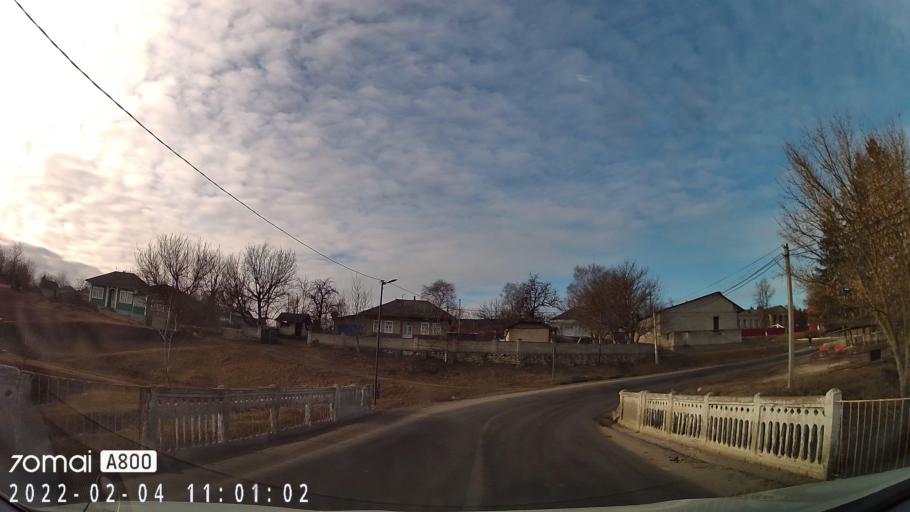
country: RO
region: Botosani
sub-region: Comuna Radauti-Prut
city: Miorcani
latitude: 48.2961
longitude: 26.9371
